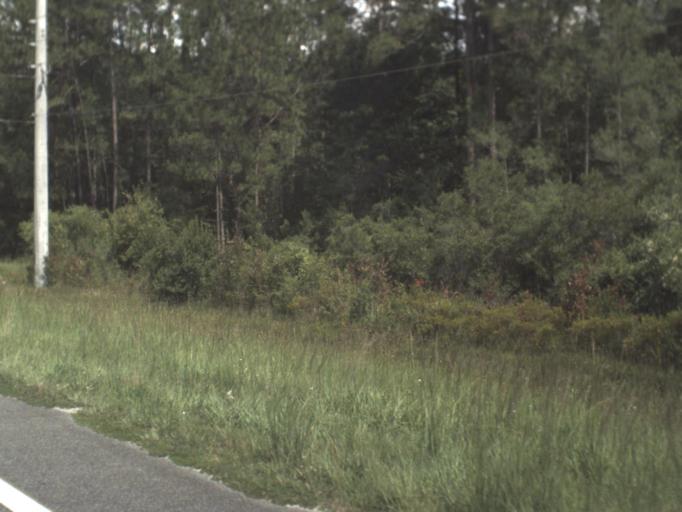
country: US
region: Florida
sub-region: Bradford County
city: Starke
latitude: 29.9548
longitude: -82.0656
